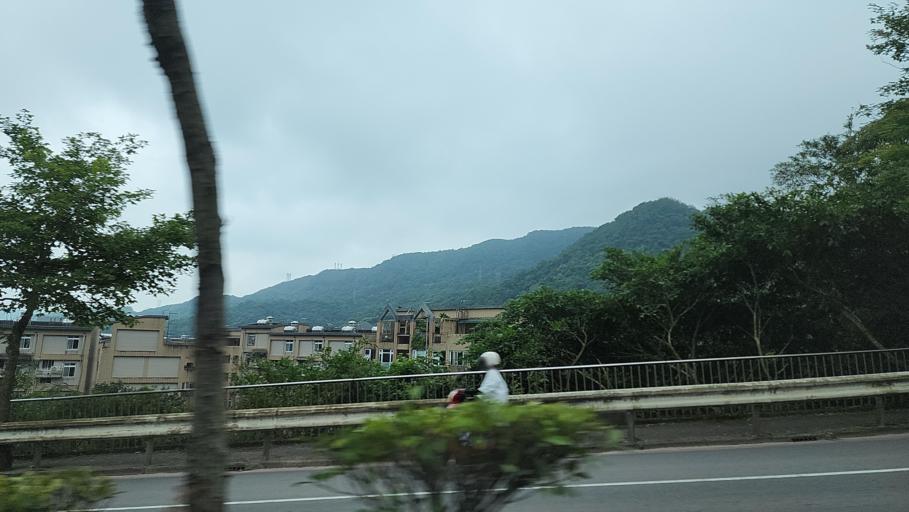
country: TW
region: Taiwan
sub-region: Keelung
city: Keelung
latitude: 25.1608
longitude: 121.6942
